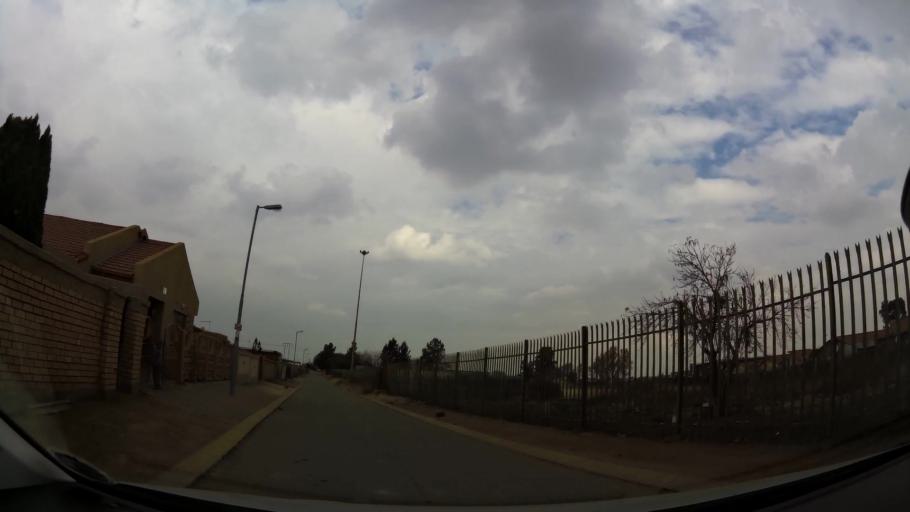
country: ZA
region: Gauteng
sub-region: City of Johannesburg Metropolitan Municipality
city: Soweto
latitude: -26.2575
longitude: 27.8581
